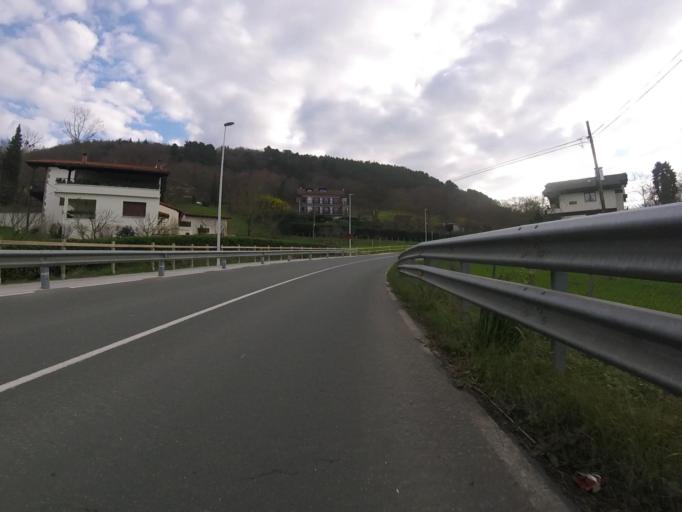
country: ES
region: Basque Country
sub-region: Provincia de Guipuzcoa
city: Irun
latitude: 43.3251
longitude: -1.8166
